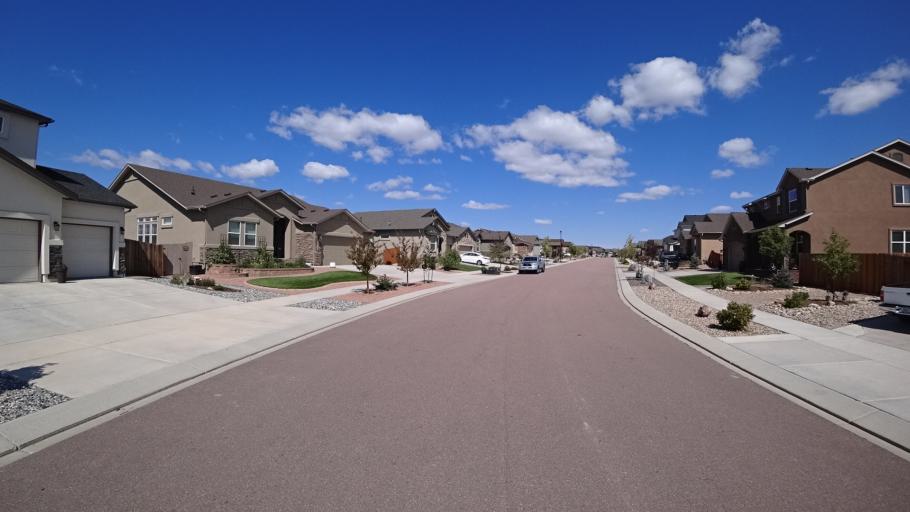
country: US
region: Colorado
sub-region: El Paso County
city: Cimarron Hills
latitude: 38.9329
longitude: -104.6847
